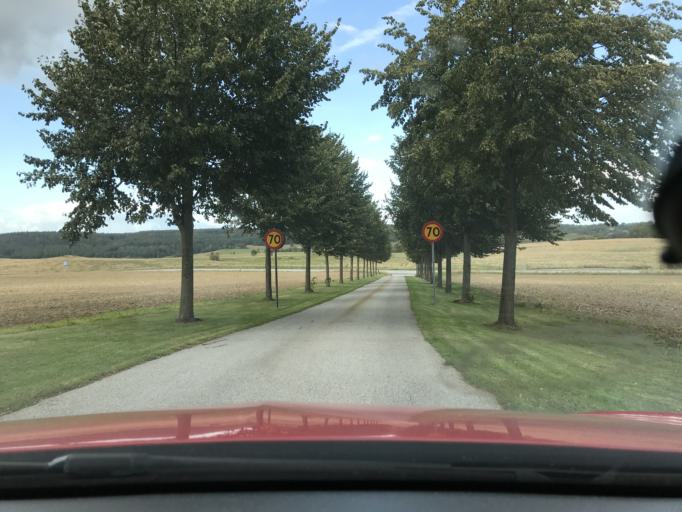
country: SE
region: Skane
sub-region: Simrishamns Kommun
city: Kivik
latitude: 55.7143
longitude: 14.1516
